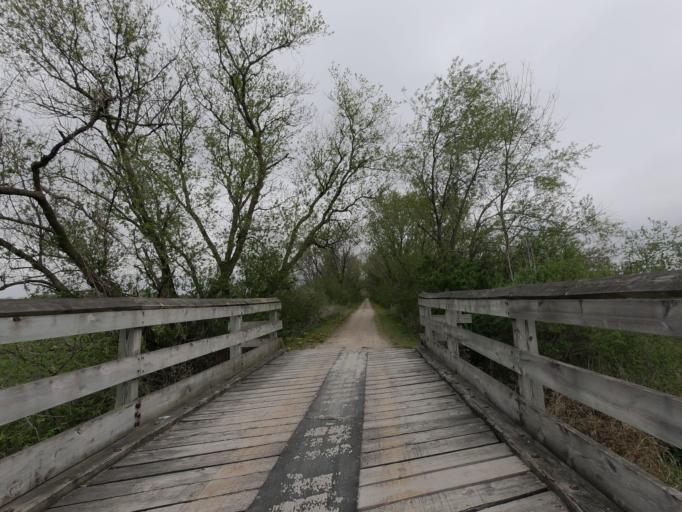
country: US
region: Wisconsin
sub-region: Jefferson County
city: Johnson Creek
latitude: 43.0303
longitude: -88.7452
